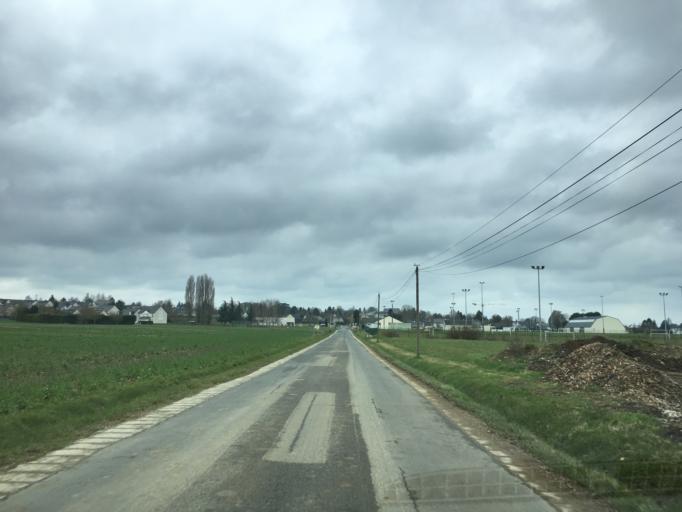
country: FR
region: Centre
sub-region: Departement d'Indre-et-Loire
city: Chanceaux-sur-Choisille
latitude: 47.4736
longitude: 0.7131
